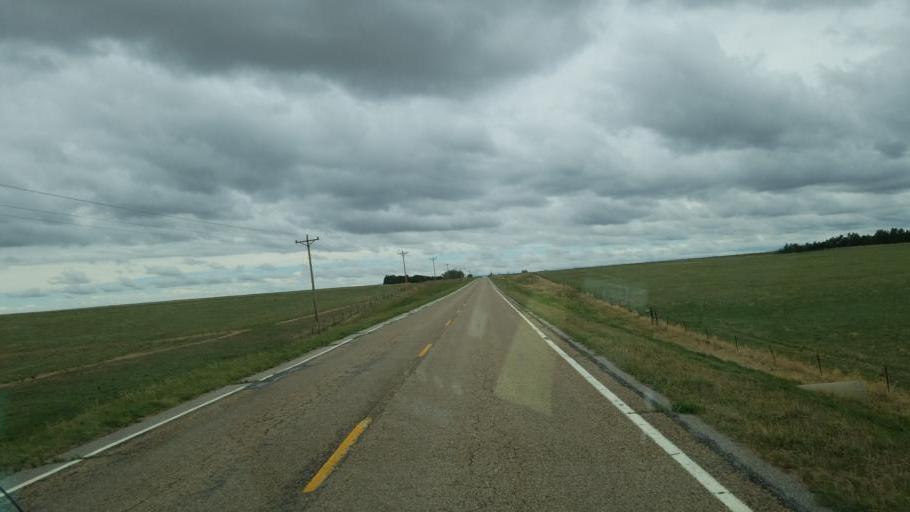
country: US
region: Colorado
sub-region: El Paso County
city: Ellicott
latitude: 38.8397
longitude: -103.9613
